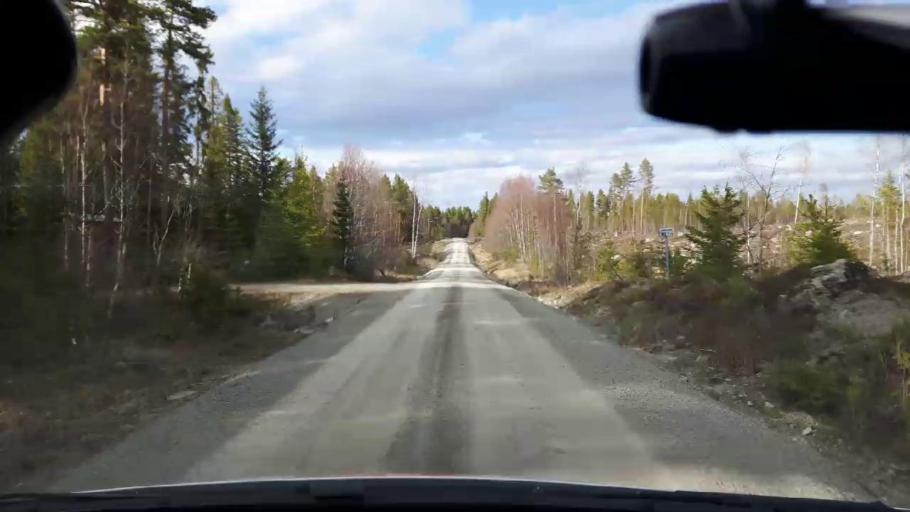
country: SE
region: Jaemtland
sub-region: Bergs Kommun
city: Hoverberg
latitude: 62.9190
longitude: 14.6390
